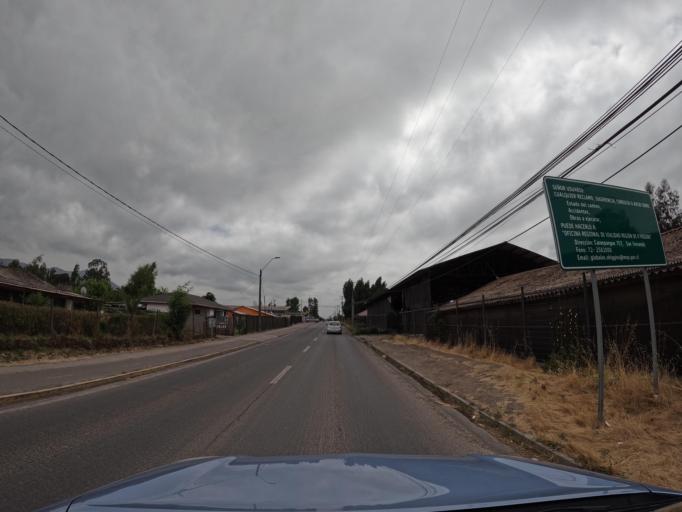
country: CL
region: O'Higgins
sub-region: Provincia de Colchagua
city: Chimbarongo
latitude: -34.7174
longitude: -71.0499
